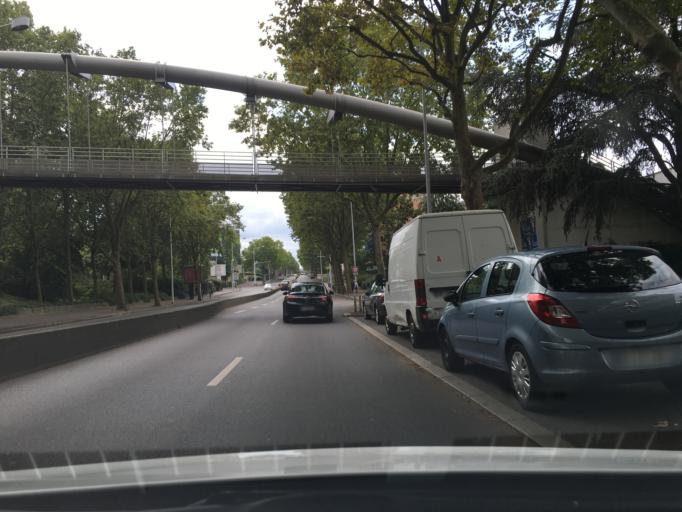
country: FR
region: Ile-de-France
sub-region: Departement des Hauts-de-Seine
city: Nanterre
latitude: 48.8948
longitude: 2.2137
